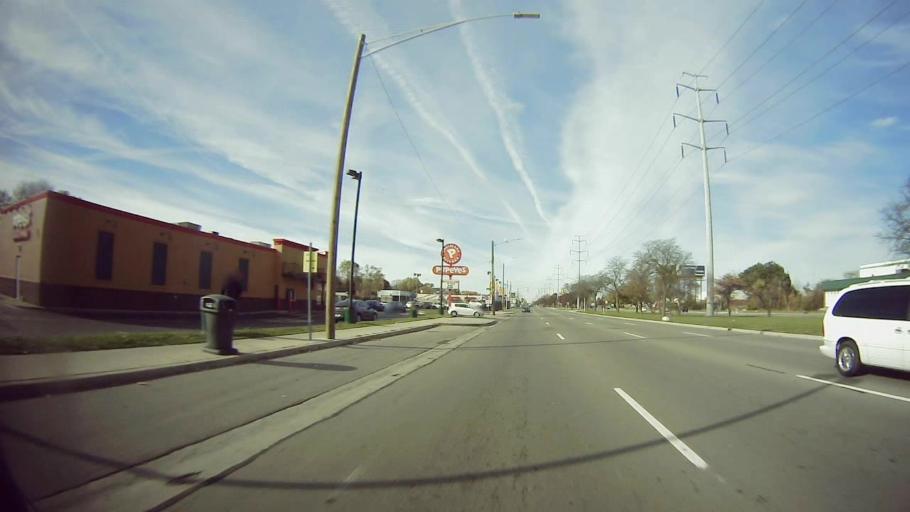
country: US
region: Michigan
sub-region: Oakland County
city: Southfield
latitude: 42.4434
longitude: -83.2494
